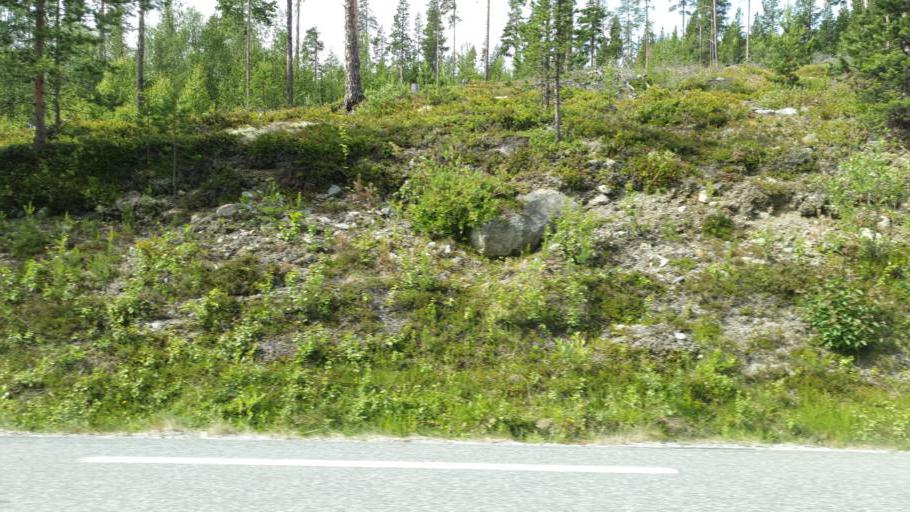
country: NO
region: Oppland
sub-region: Vaga
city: Vagamo
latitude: 61.7387
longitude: 9.0914
